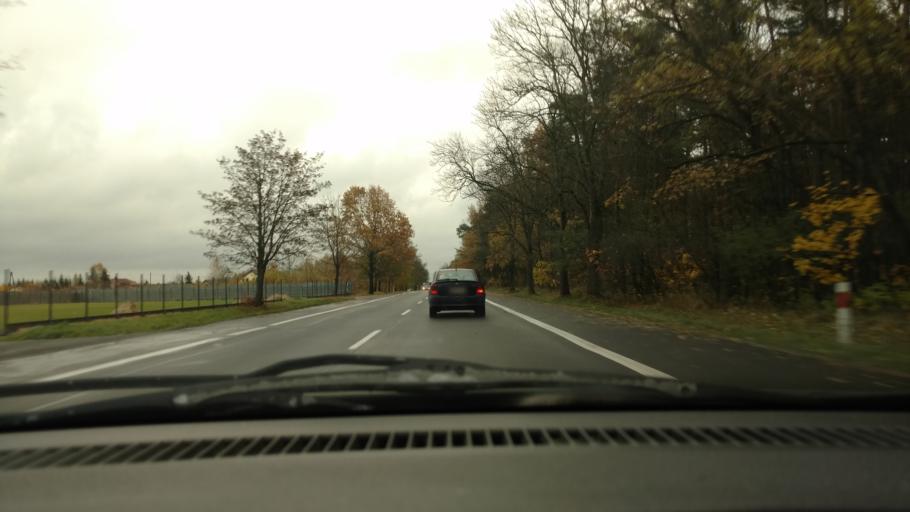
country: PL
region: Lodz Voivodeship
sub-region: Powiat laski
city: Lask
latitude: 51.5967
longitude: 19.0862
